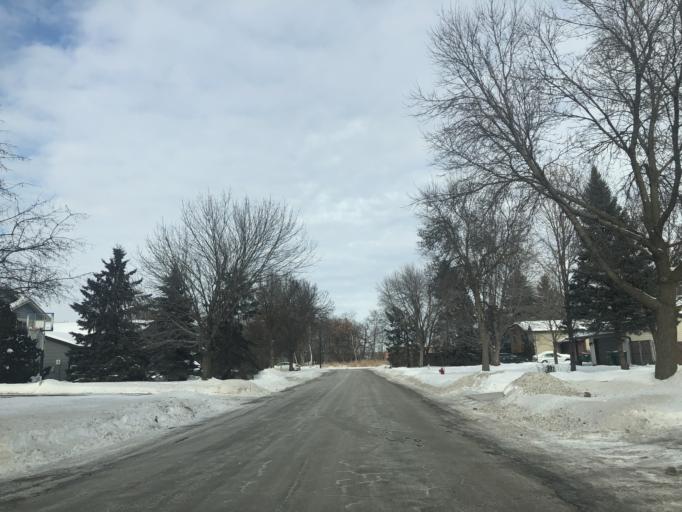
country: US
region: Minnesota
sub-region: Anoka County
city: Circle Pines
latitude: 45.1557
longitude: -93.1601
